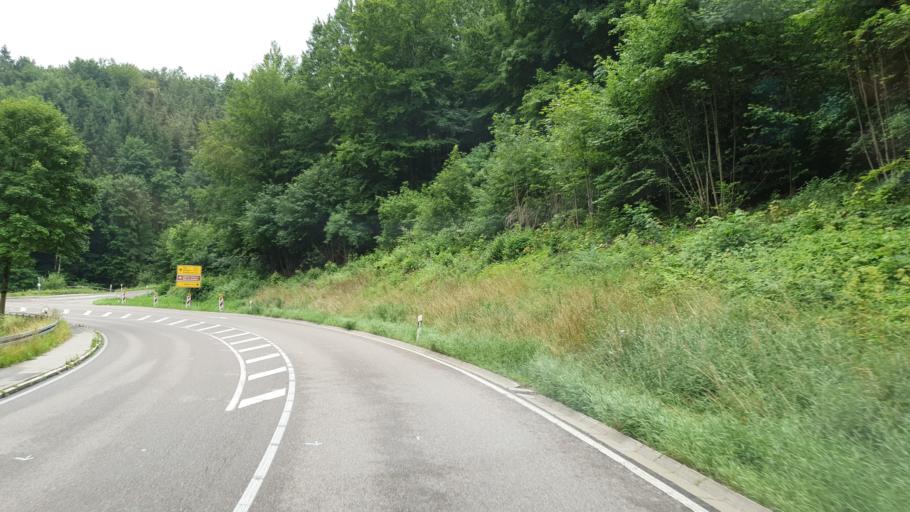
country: DE
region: Baden-Wuerttemberg
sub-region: Tuebingen Region
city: Blaubeuren
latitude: 48.4223
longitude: 9.7649
